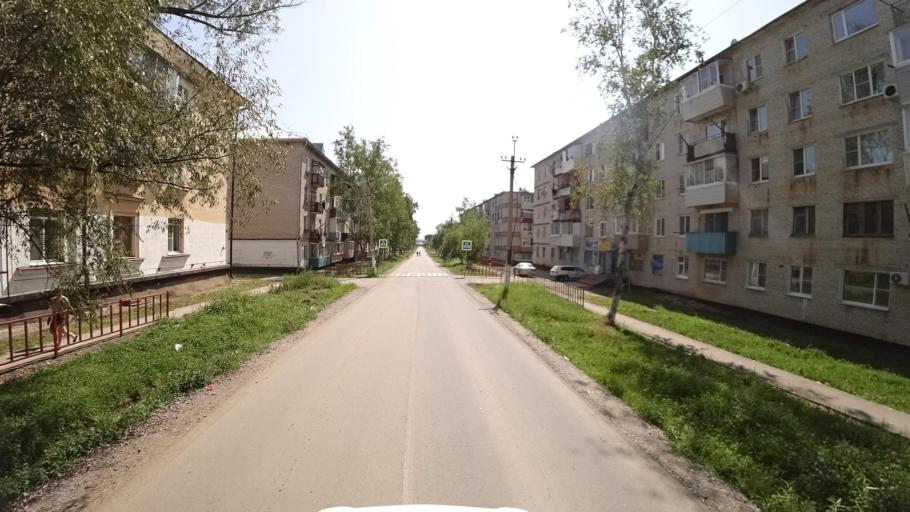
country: RU
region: Khabarovsk Krai
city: Khor
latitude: 47.9669
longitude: 135.1166
